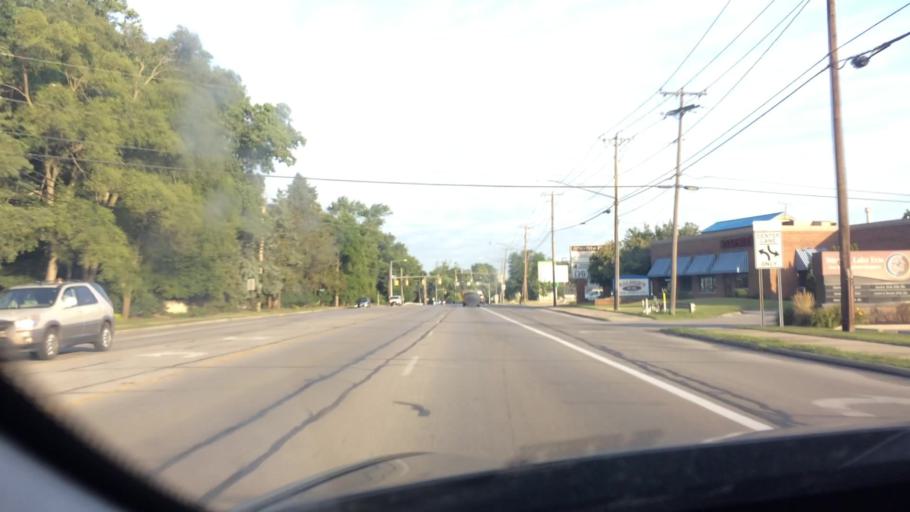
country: US
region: Ohio
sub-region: Lucas County
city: Sylvania
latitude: 41.7093
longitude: -83.6750
